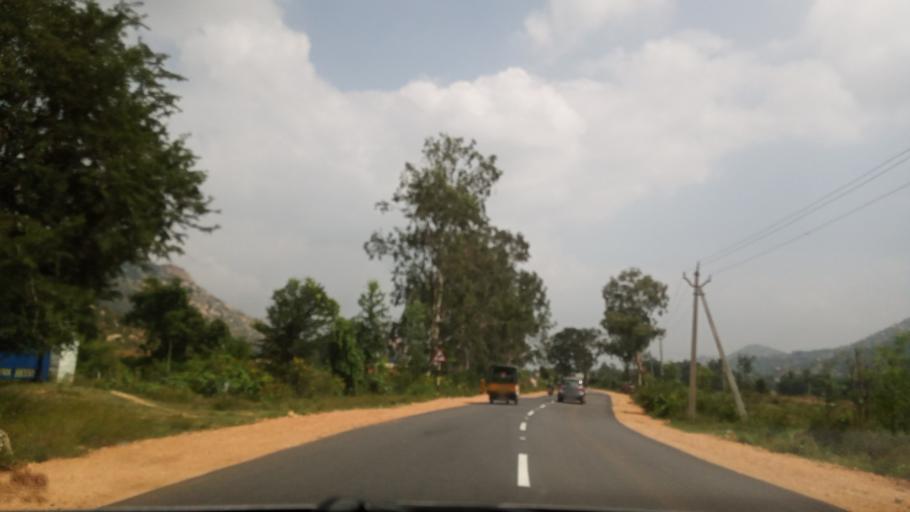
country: IN
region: Andhra Pradesh
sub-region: Chittoor
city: Madanapalle
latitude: 13.6363
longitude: 78.5974
